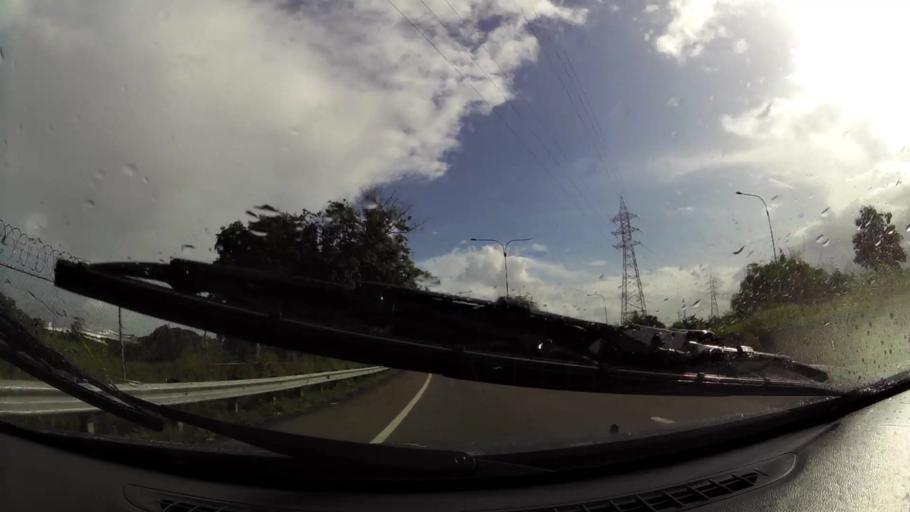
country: TT
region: Tunapuna/Piarco
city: Tunapuna
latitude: 10.6375
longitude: -61.4313
